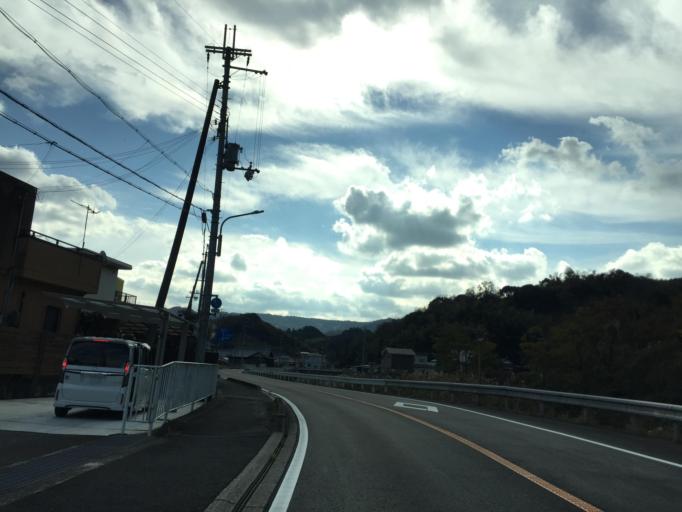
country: JP
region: Wakayama
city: Kainan
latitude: 34.1708
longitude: 135.2507
